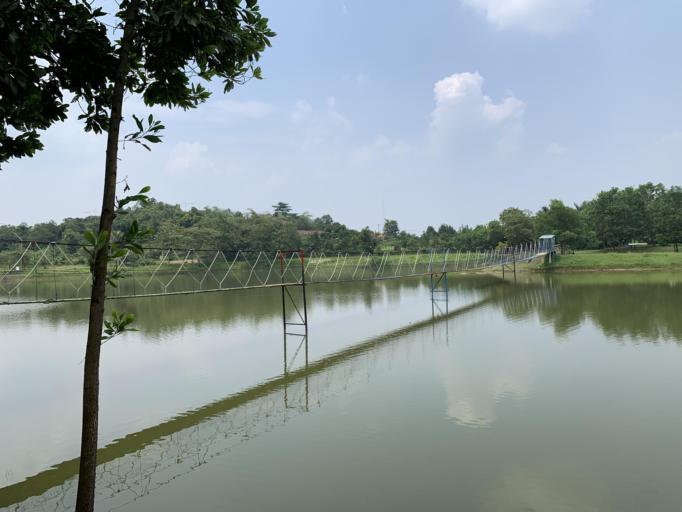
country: ID
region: West Java
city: Serpong
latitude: -6.4085
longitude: 106.5859
